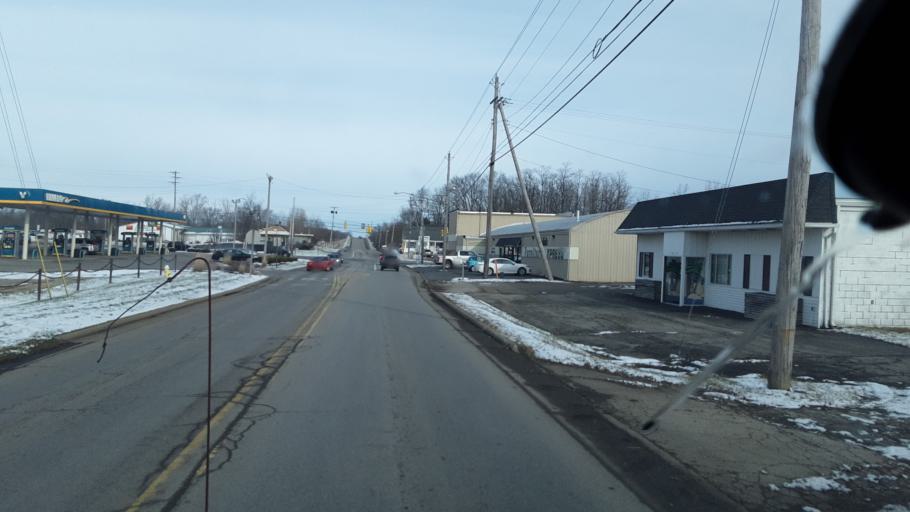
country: US
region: Ohio
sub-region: Richland County
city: Ontario
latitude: 40.7670
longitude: -82.5721
